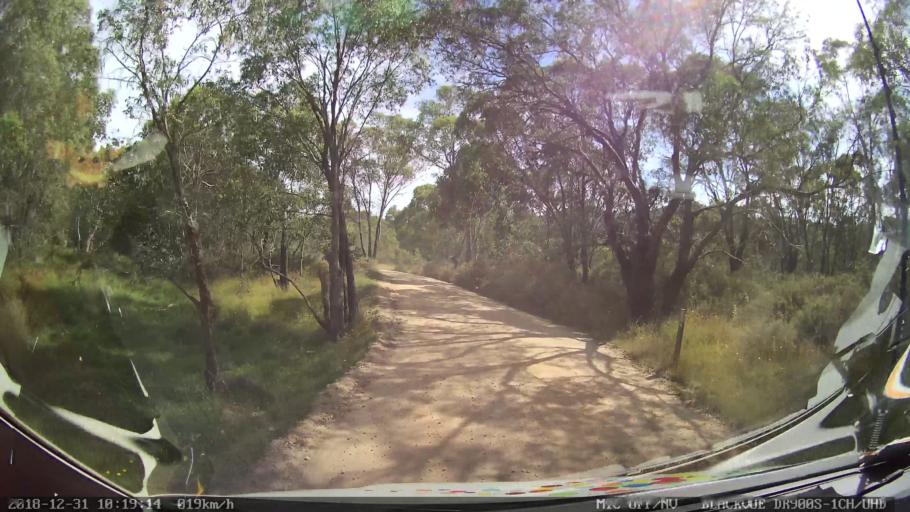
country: AU
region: New South Wales
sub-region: Snowy River
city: Jindabyne
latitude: -36.5412
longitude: 148.1346
